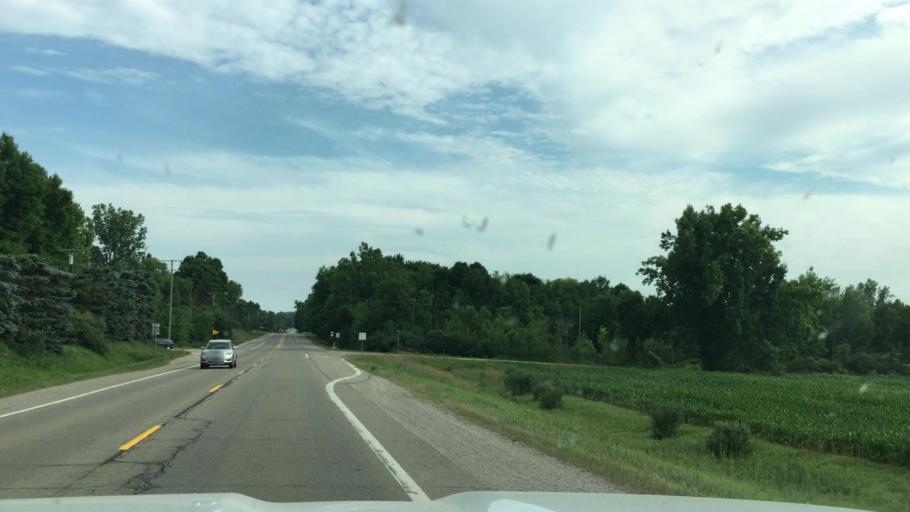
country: US
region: Michigan
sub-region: Sanilac County
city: Brown City
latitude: 43.1683
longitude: -83.0759
